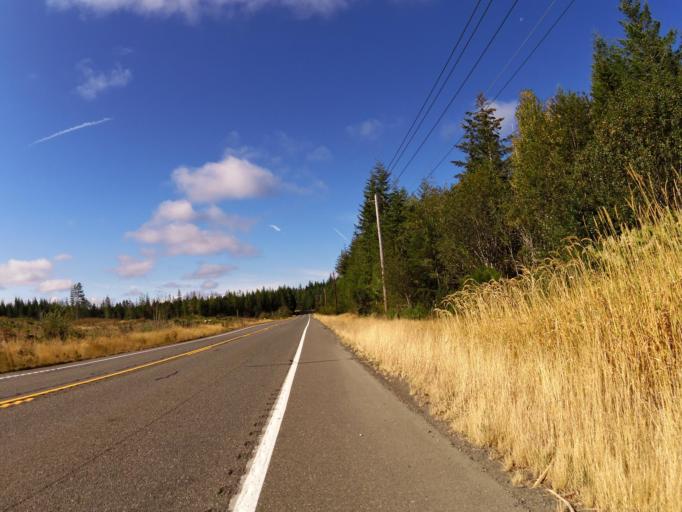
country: US
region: Washington
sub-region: Mason County
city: Allyn
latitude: 47.3224
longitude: -122.9011
